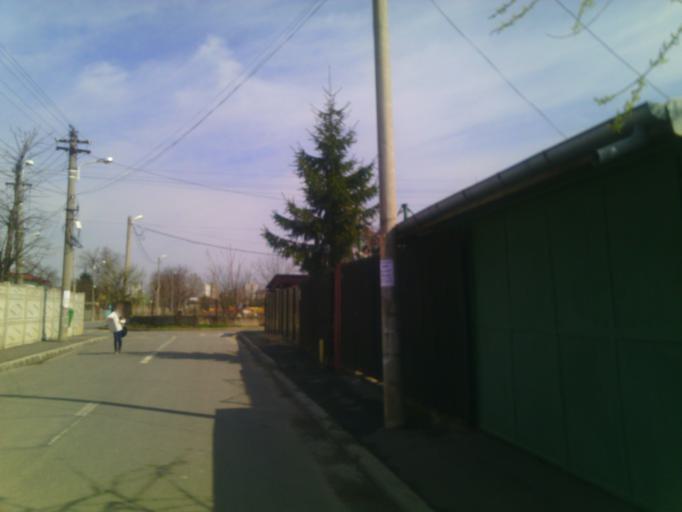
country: RO
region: Ilfov
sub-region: Comuna Jilava
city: Jilava
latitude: 44.3712
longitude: 26.1028
